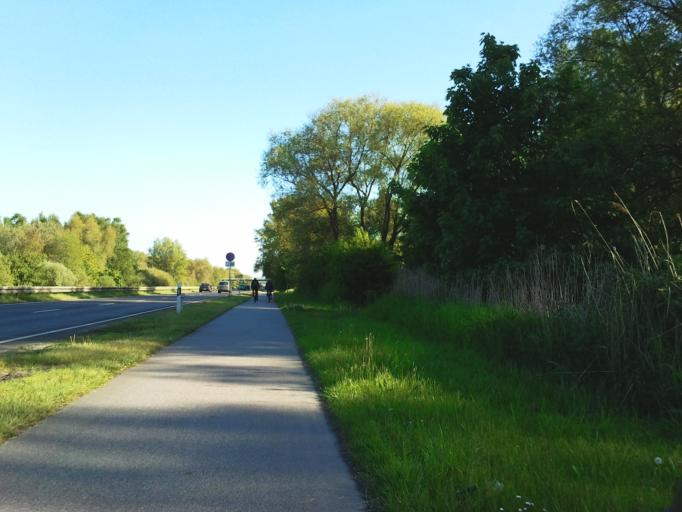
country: DE
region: Mecklenburg-Vorpommern
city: Warnemuende
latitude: 54.1276
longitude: 12.0639
